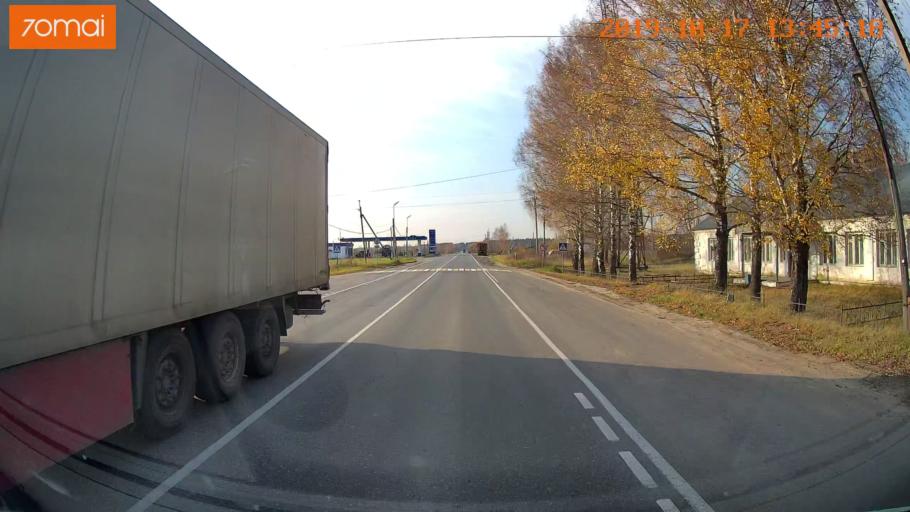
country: RU
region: Rjazan
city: Tuma
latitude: 55.1469
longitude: 40.5159
